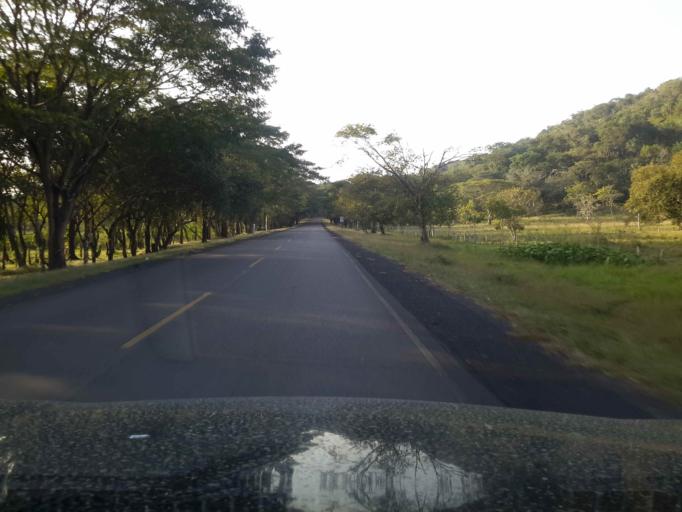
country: NI
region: Rio San Juan
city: San Miguelito
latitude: 11.3997
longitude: -84.8252
